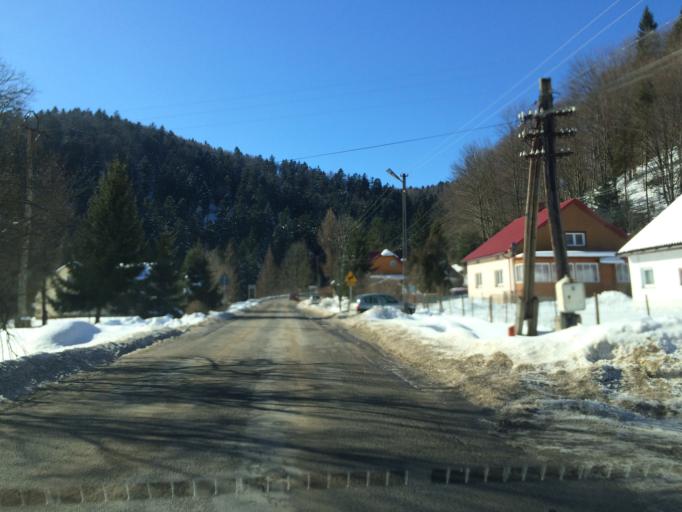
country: PL
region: Subcarpathian Voivodeship
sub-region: Powiat leski
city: Cisna
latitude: 49.2077
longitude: 22.3239
